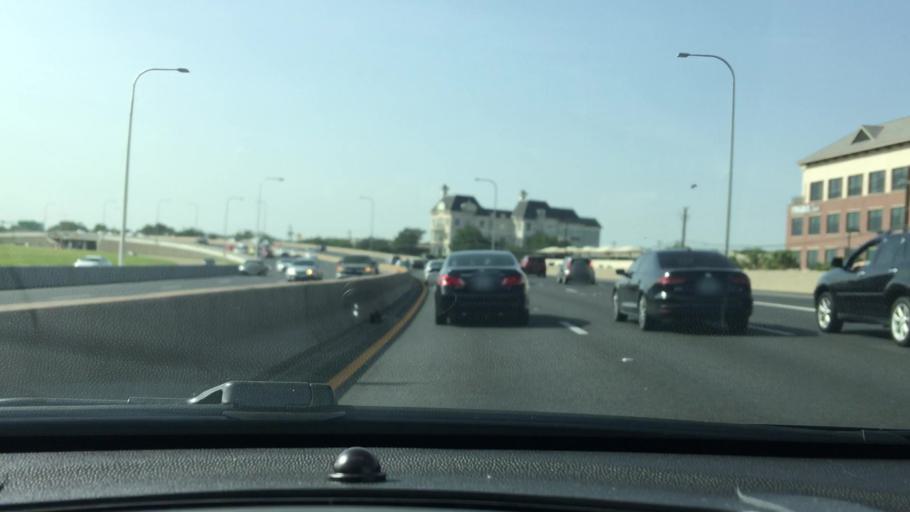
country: US
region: Texas
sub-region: Dallas County
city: Addison
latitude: 32.9726
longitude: -96.8215
